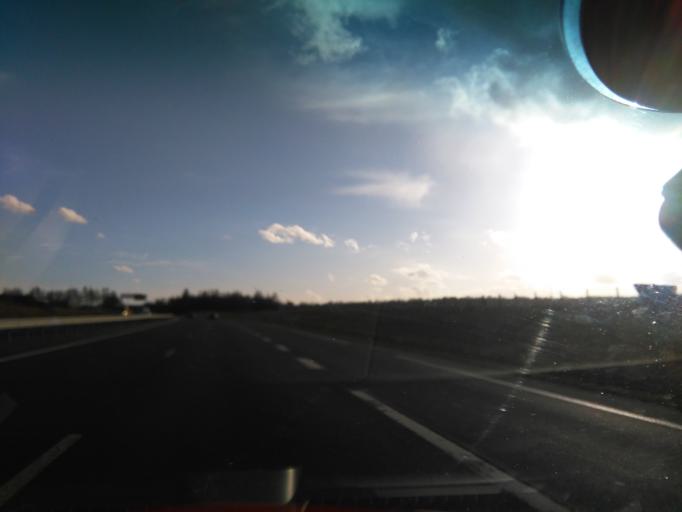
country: FR
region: Lower Normandy
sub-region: Departement du Calvados
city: Falaise
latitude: 48.9111
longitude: -0.2108
